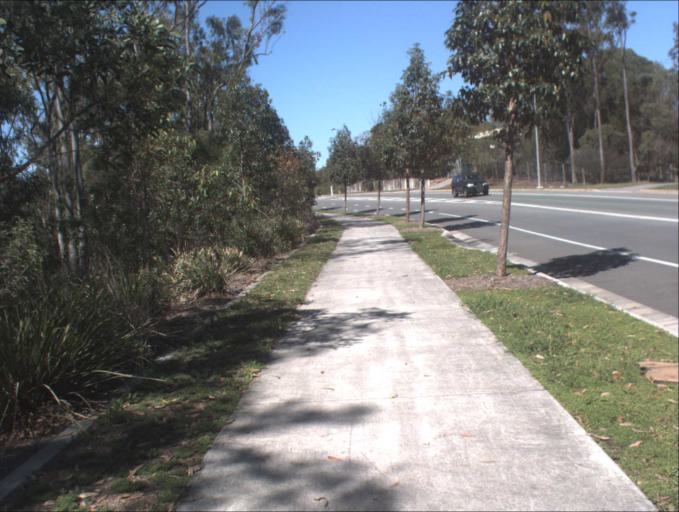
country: AU
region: Queensland
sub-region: Logan
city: Waterford West
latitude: -27.7135
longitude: 153.1594
